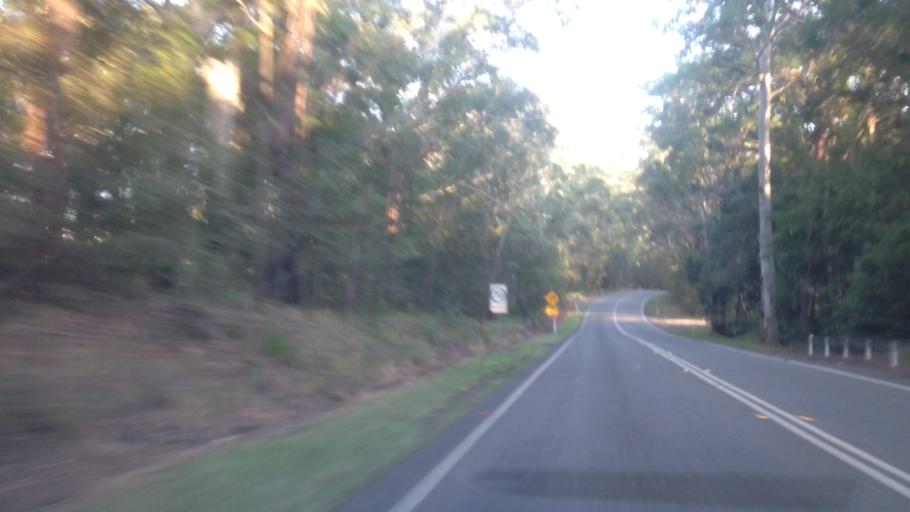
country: AU
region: New South Wales
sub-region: Lake Macquarie Shire
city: Cooranbong
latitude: -32.9770
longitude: 151.4831
